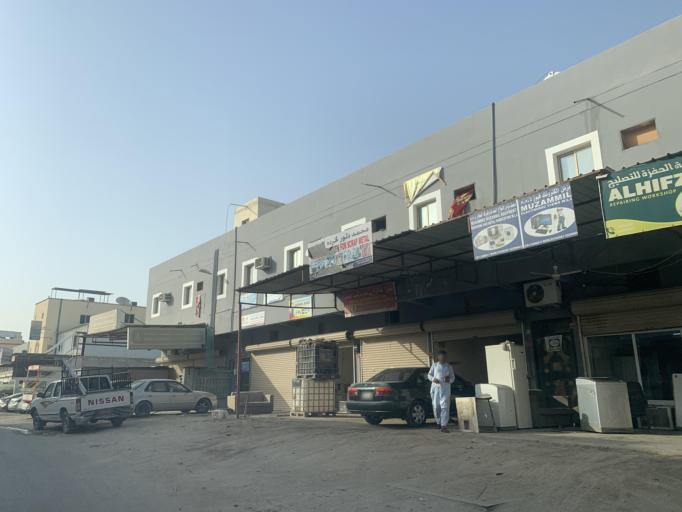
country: BH
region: Central Governorate
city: Madinat Hamad
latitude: 26.1451
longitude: 50.4863
